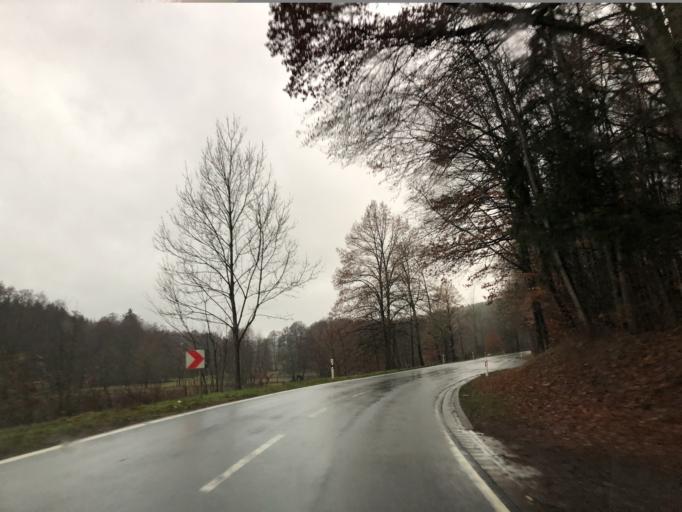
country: DE
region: Hesse
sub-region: Regierungsbezirk Darmstadt
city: Bad Konig
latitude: 49.7372
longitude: 9.0402
